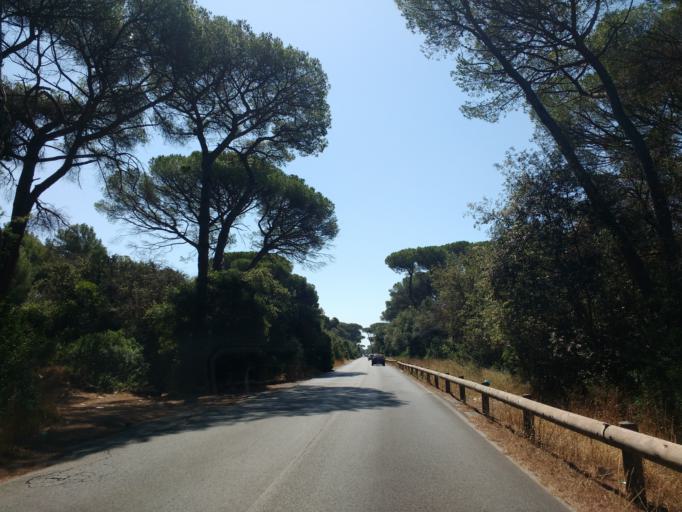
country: IT
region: Latium
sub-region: Citta metropolitana di Roma Capitale
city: Acilia-Castel Fusano-Ostia Antica
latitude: 41.7233
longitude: 12.3446
